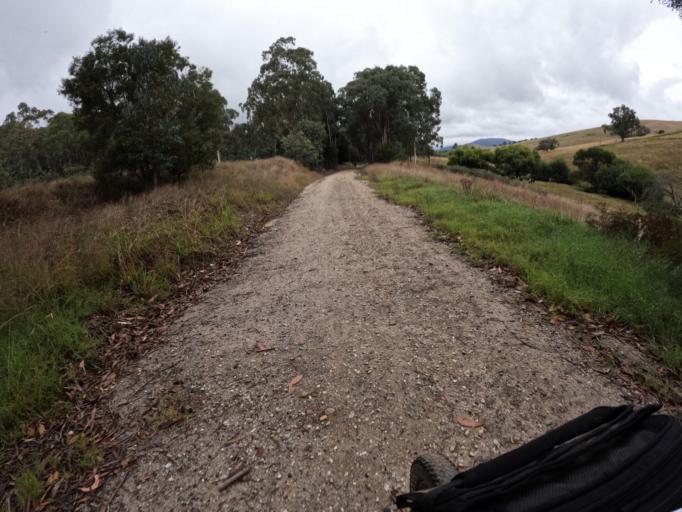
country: AU
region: New South Wales
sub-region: Greater Hume Shire
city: Holbrook
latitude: -36.1589
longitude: 147.4102
